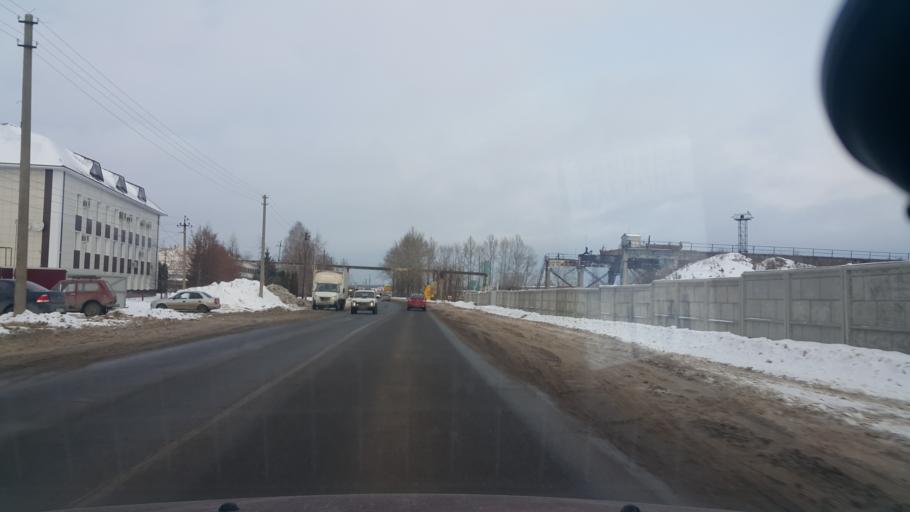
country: RU
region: Tambov
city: Pokrovo-Prigorodnoye
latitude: 52.6566
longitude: 41.4278
